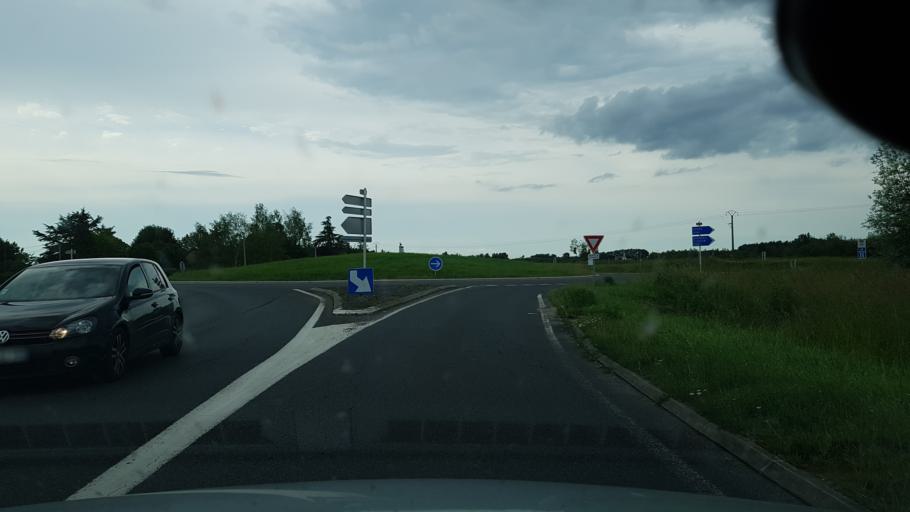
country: FR
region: Centre
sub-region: Departement du Loir-et-Cher
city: Chatillon-sur-Cher
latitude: 47.3202
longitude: 1.4968
